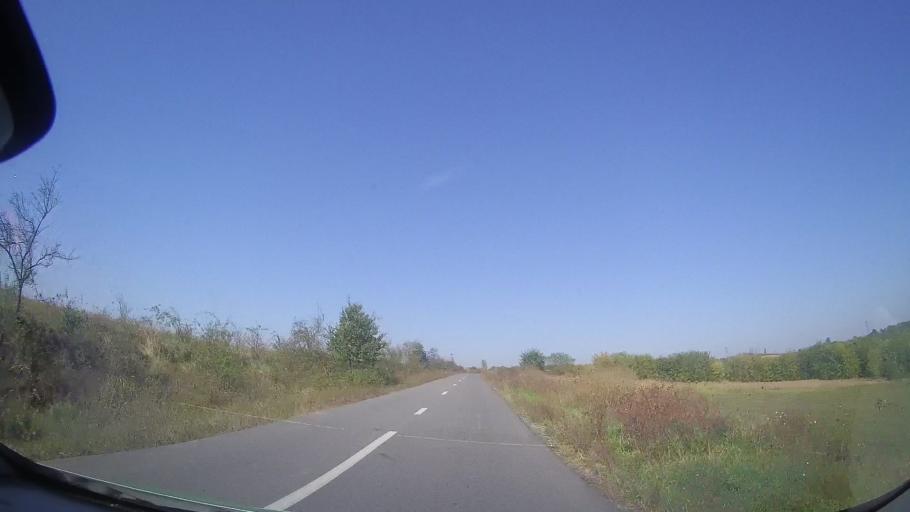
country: RO
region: Timis
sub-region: Comuna Balint
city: Balint
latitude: 45.8211
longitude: 21.8518
